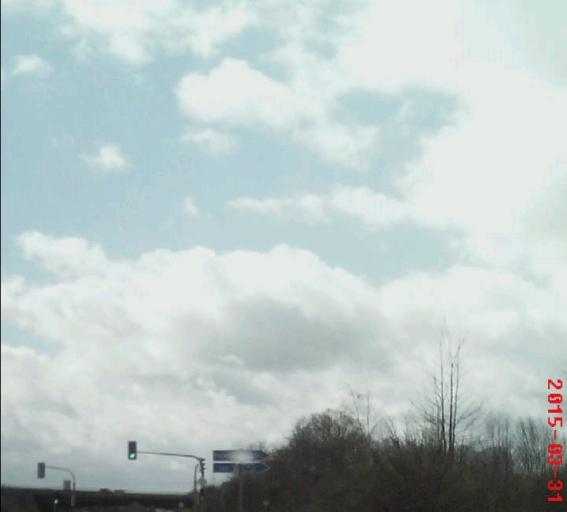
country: DE
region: Thuringia
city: Kirchheim
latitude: 50.9084
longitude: 11.0107
